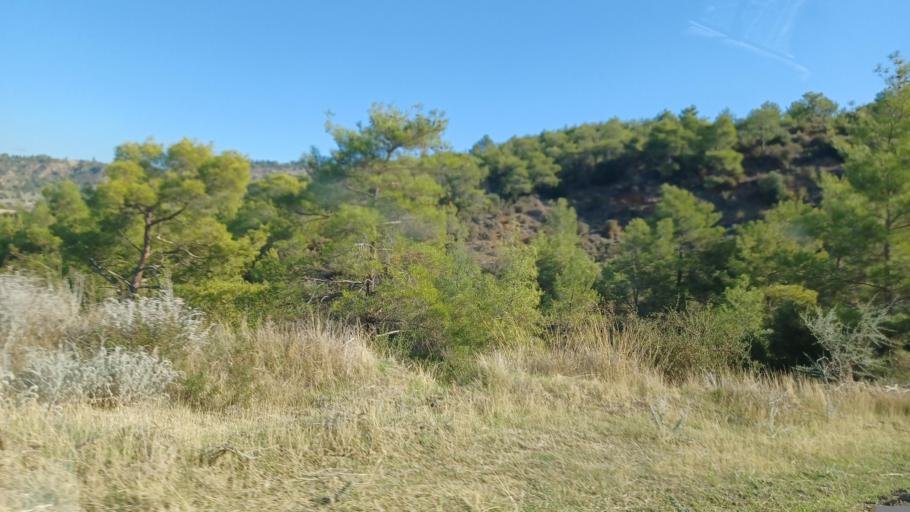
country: CY
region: Pafos
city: Polis
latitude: 35.0223
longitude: 32.4917
